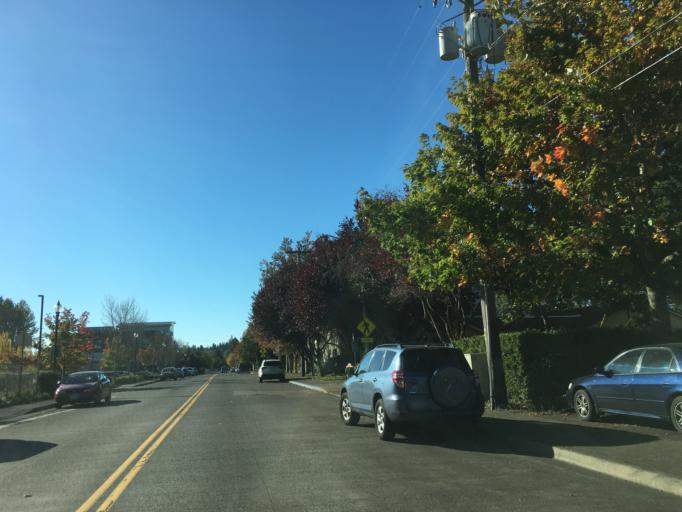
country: US
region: Oregon
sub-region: Multnomah County
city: Gresham
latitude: 45.5030
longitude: -122.4224
